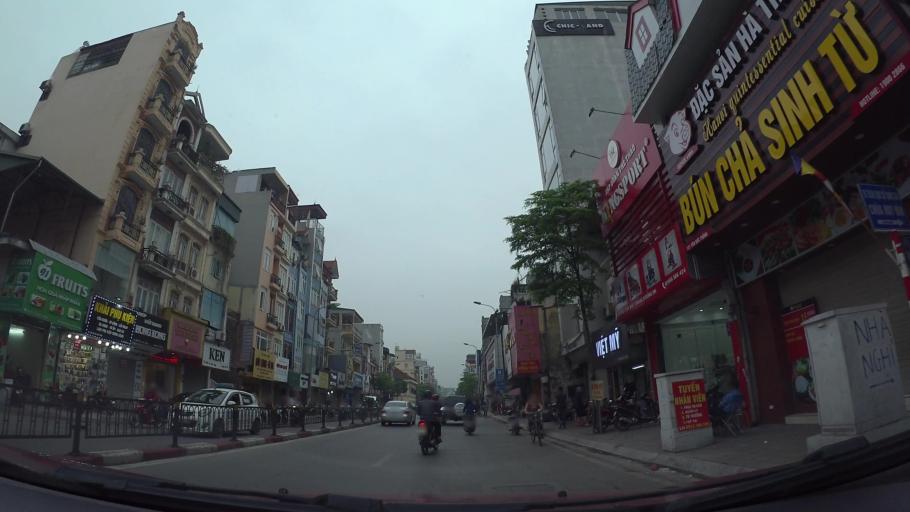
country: VN
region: Ha Noi
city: Dong Da
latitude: 21.0236
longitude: 105.8323
